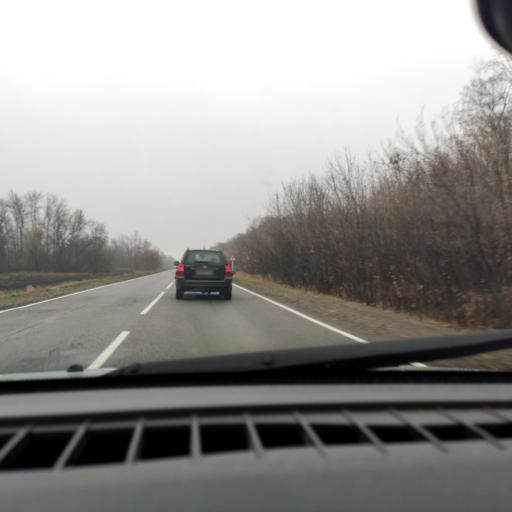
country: RU
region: Voronezj
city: Shilovo
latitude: 51.4116
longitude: 39.0048
